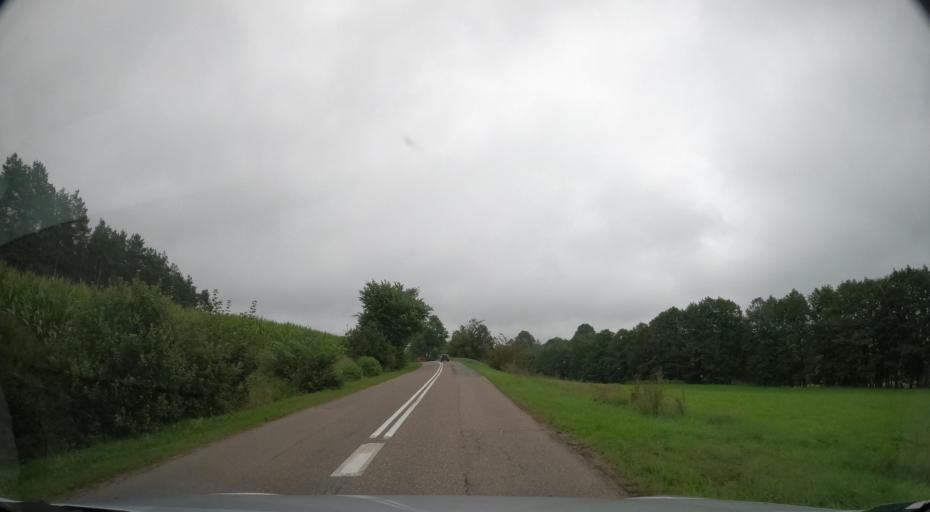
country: PL
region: Pomeranian Voivodeship
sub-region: Powiat wejherowski
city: Luzino
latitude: 54.4821
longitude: 18.1023
